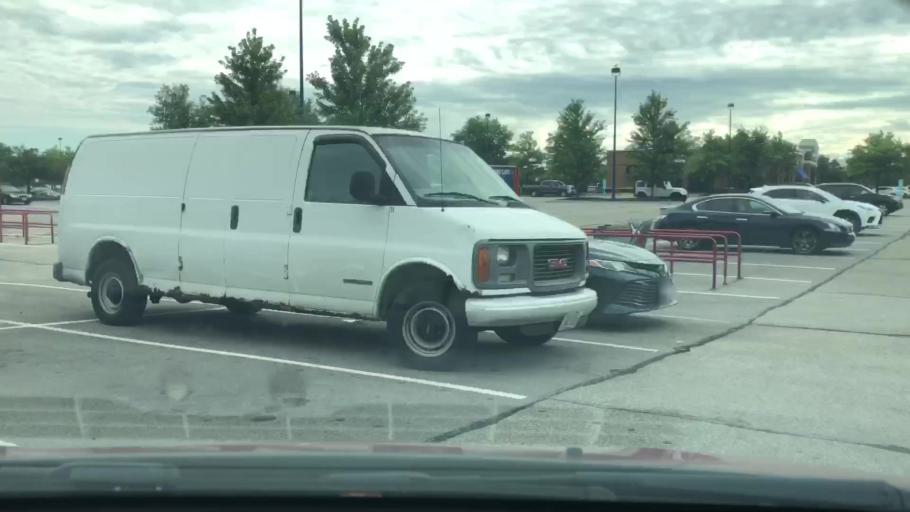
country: US
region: Ohio
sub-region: Franklin County
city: Minerva Park
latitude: 40.0551
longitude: -82.9210
